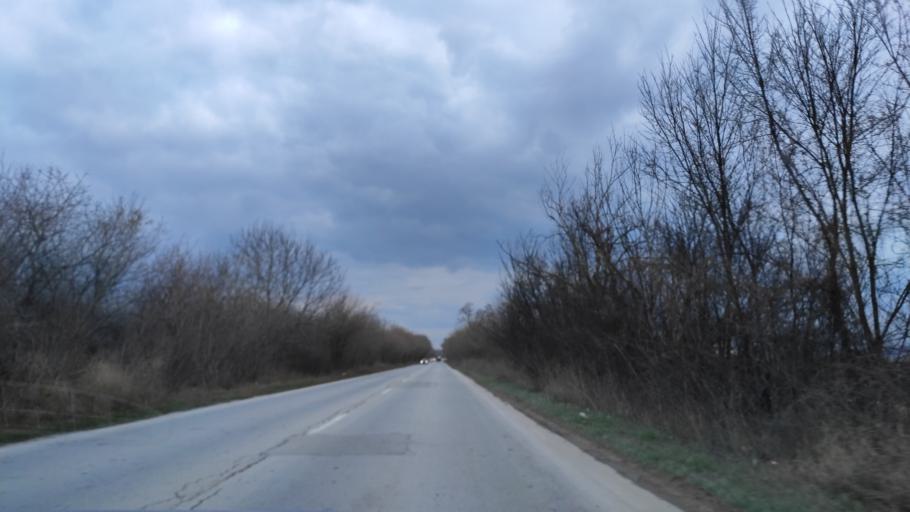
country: BG
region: Varna
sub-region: Obshtina Aksakovo
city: Aksakovo
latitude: 43.2287
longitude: 27.8368
